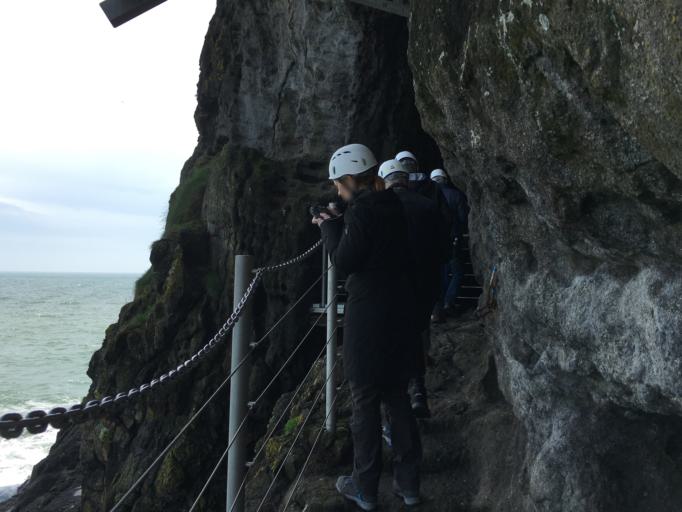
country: GB
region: Northern Ireland
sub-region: Carrickfergus District
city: Whitehead
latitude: 54.8065
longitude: -5.6914
